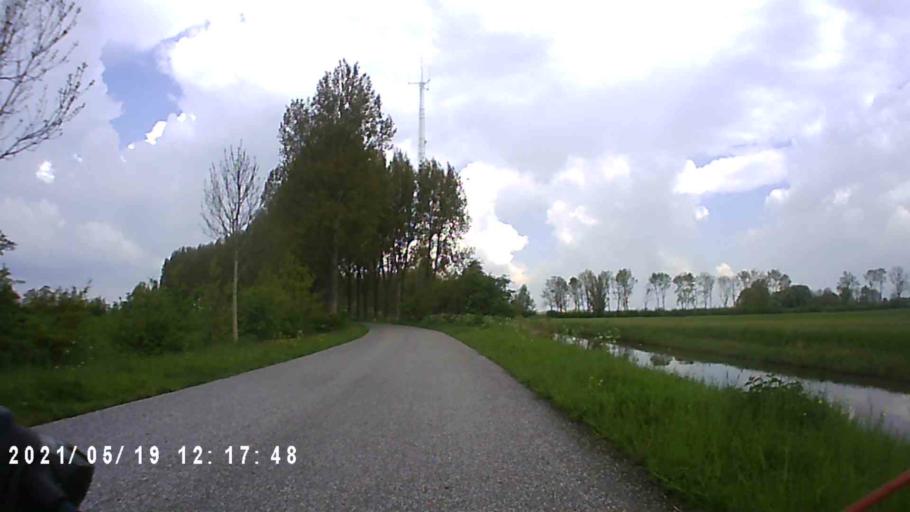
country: NL
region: Friesland
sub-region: Gemeente Kollumerland en Nieuwkruisland
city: Kollum
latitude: 53.2592
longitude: 6.1744
